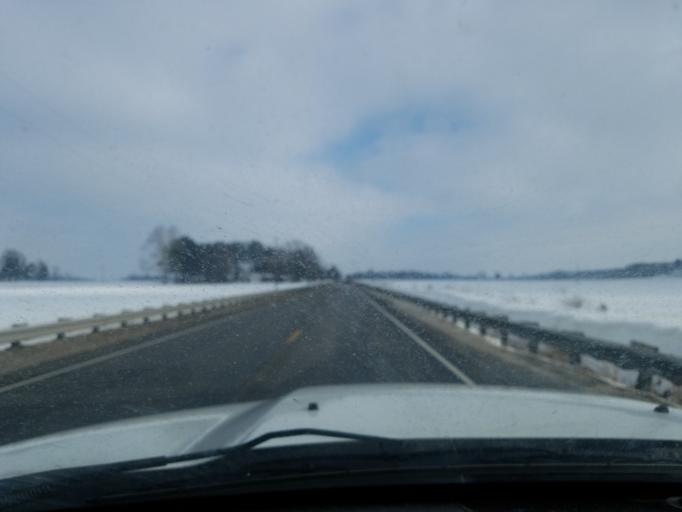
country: US
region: Indiana
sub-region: Marshall County
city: Plymouth
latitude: 41.4498
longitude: -86.2791
